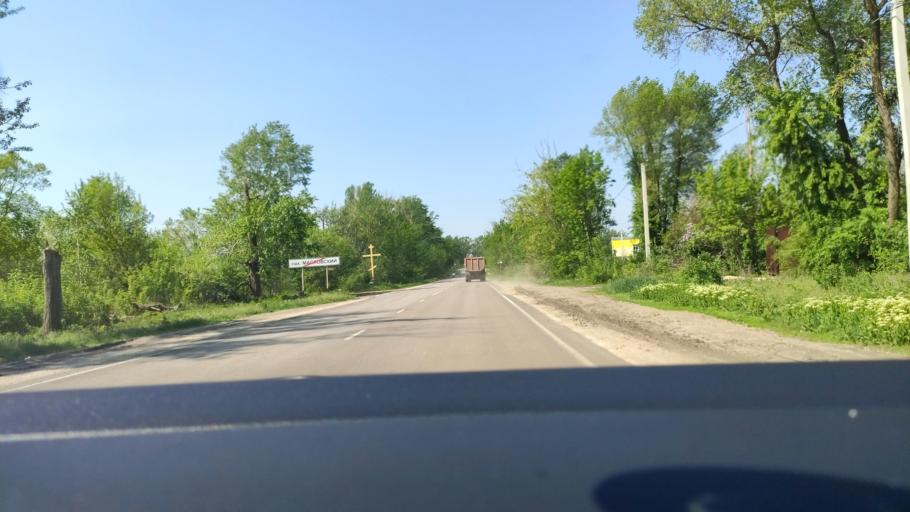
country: RU
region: Voronezj
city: Maslovka
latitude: 51.5320
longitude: 39.3151
